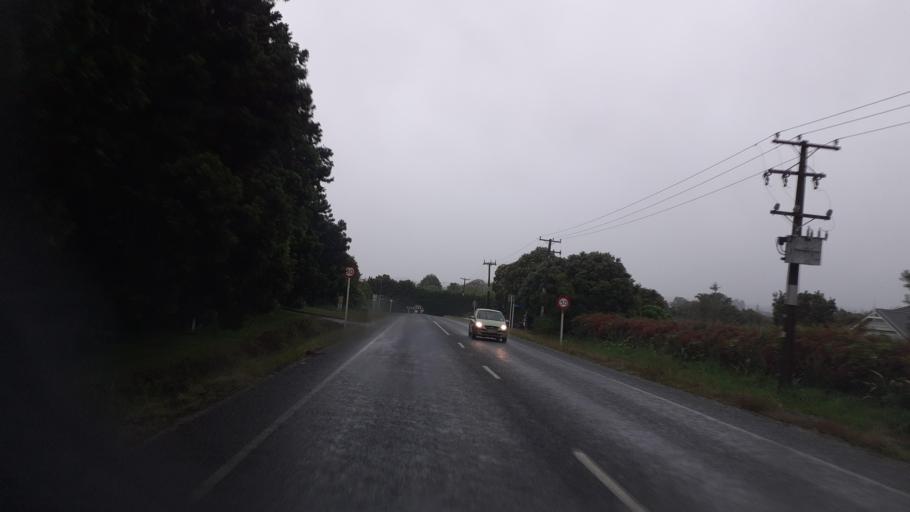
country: NZ
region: Northland
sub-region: Far North District
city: Kerikeri
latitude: -35.2108
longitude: 173.9613
